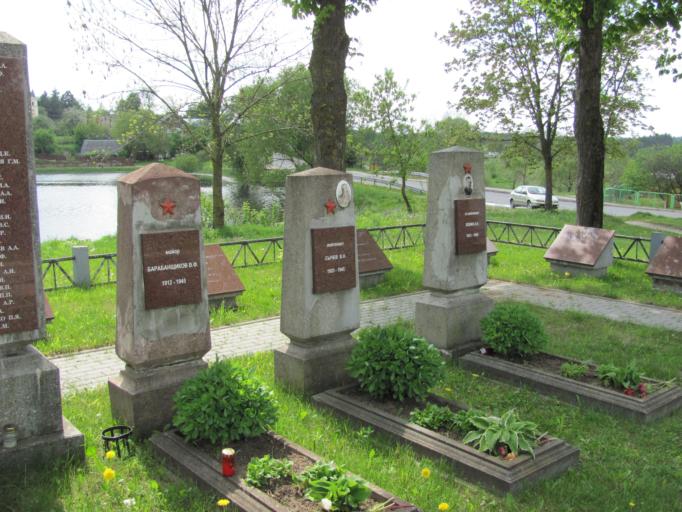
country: LT
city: Nemencine
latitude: 54.7020
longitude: 25.5198
